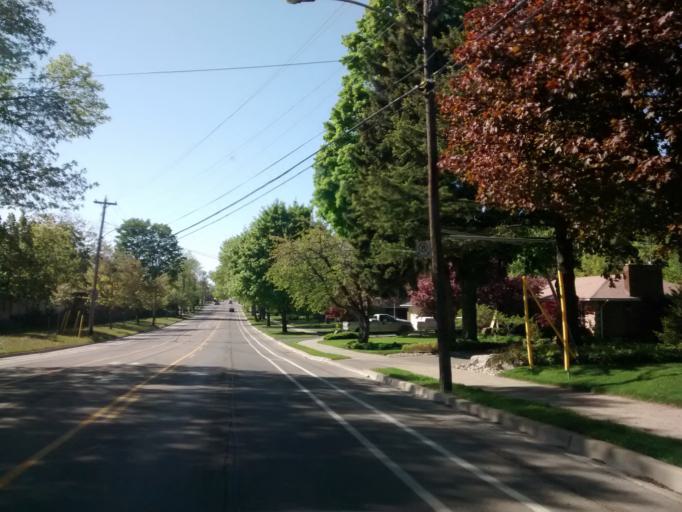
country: CA
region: Ontario
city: Burlington
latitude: 43.3613
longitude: -79.7457
